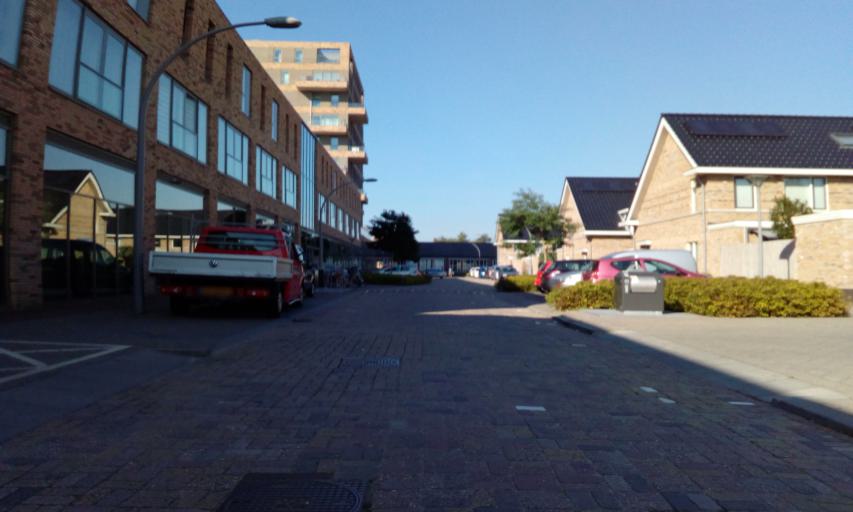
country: NL
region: South Holland
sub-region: Gemeente Vlaardingen
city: Vlaardingen
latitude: 51.9175
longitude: 4.3603
